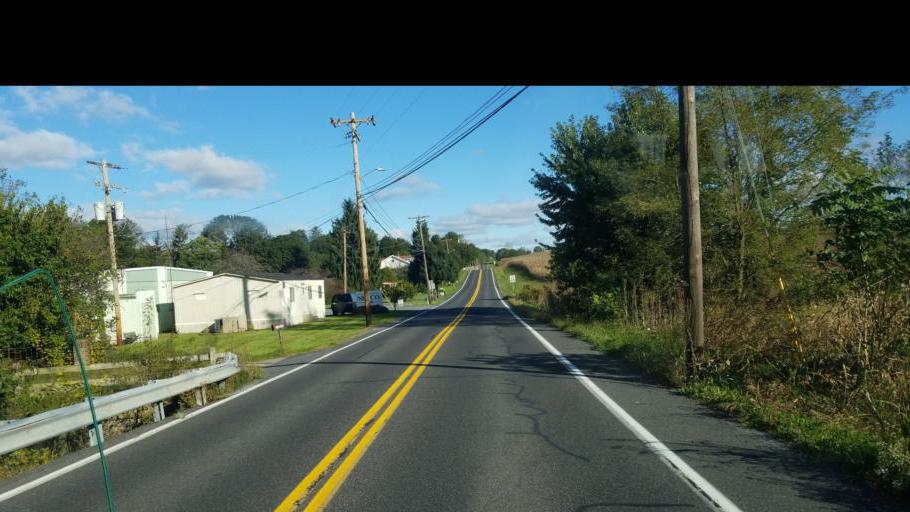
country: US
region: Pennsylvania
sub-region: Franklin County
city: Mont Alto
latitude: 39.8453
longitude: -77.5591
